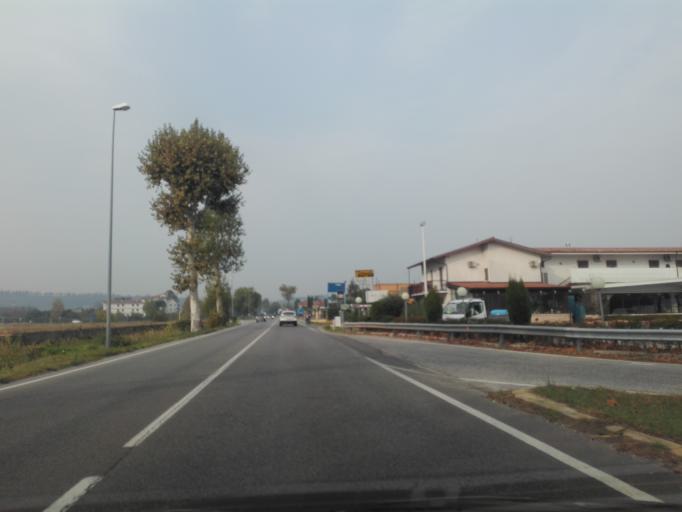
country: IT
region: Veneto
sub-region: Provincia di Verona
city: Sona
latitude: 45.4461
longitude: 10.8559
